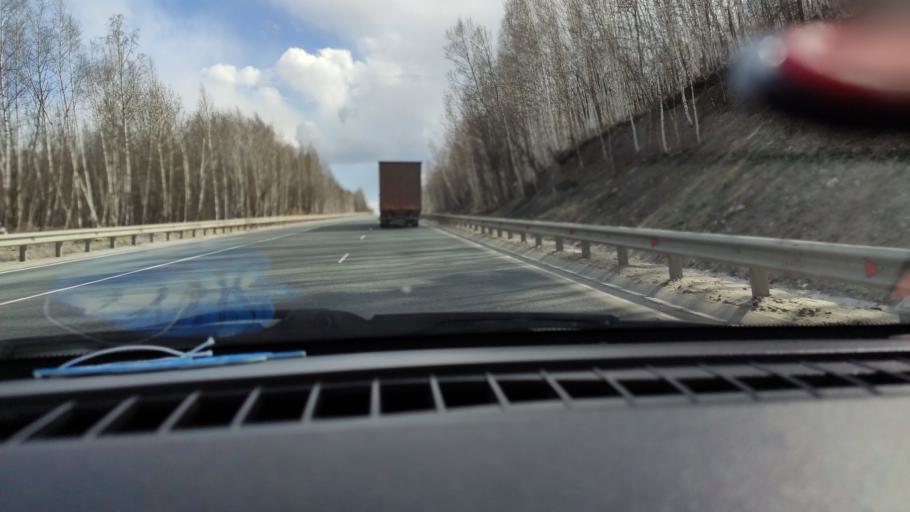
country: RU
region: Saratov
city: Khvalynsk
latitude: 52.4988
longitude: 48.0147
